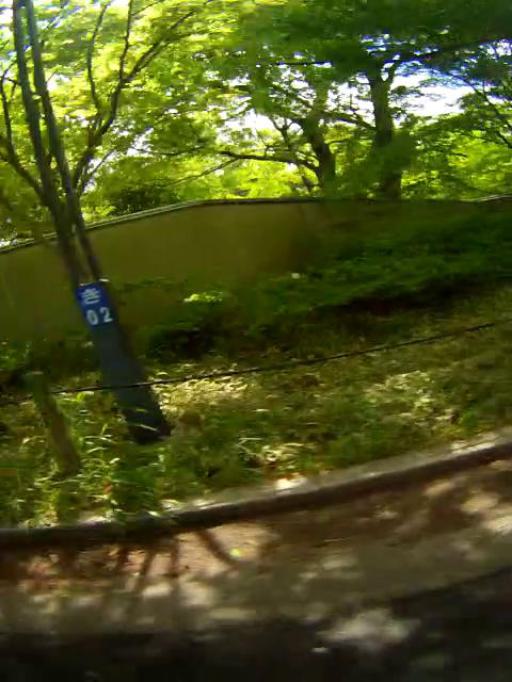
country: JP
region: Osaka
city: Osaka-shi
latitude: 34.7094
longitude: 135.5199
